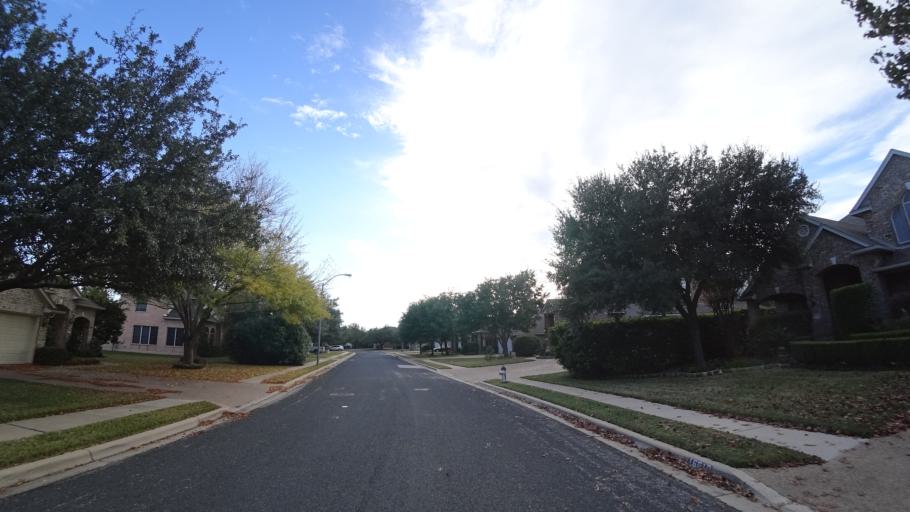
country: US
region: Texas
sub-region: Williamson County
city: Brushy Creek
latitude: 30.5049
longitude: -97.7379
